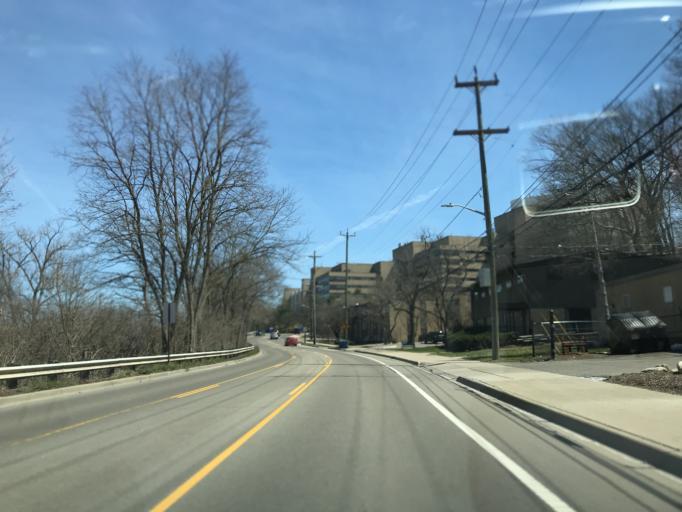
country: US
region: Michigan
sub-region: Washtenaw County
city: Ann Arbor
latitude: 42.2858
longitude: -83.7376
